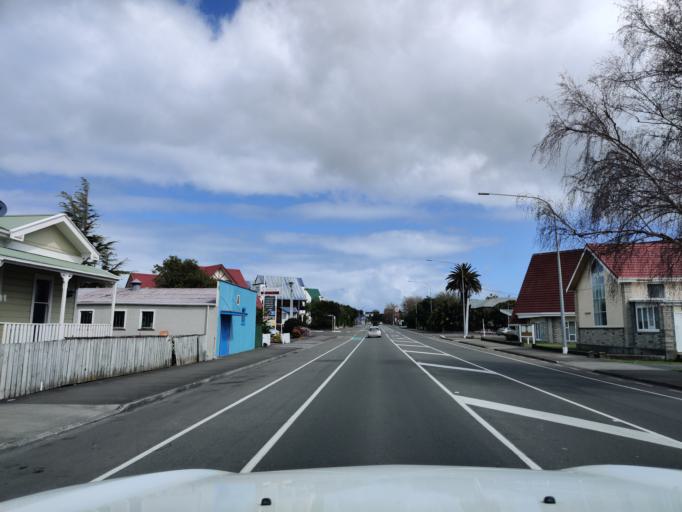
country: NZ
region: Manawatu-Wanganui
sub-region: Wanganui District
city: Wanganui
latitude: -39.9255
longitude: 175.0460
